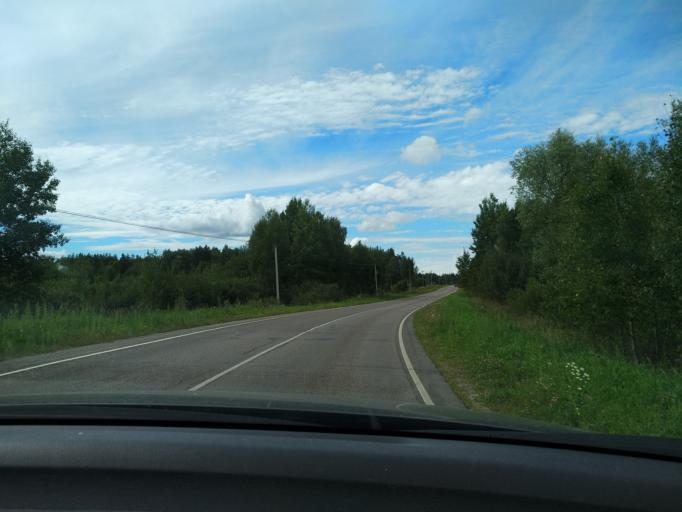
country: RU
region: Moskovskaya
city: Krasnyy Tkach
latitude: 55.3929
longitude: 39.1412
